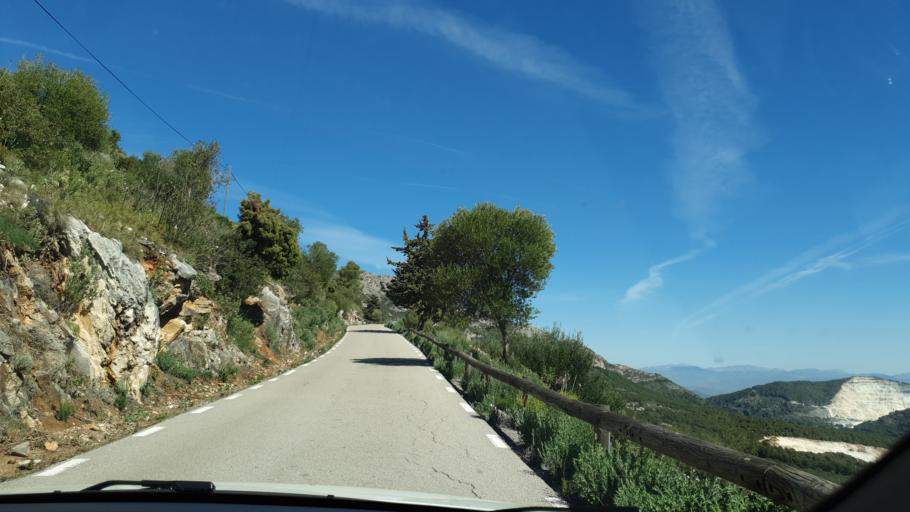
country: ES
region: Andalusia
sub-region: Provincia de Malaga
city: Ojen
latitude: 36.5890
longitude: -4.8719
